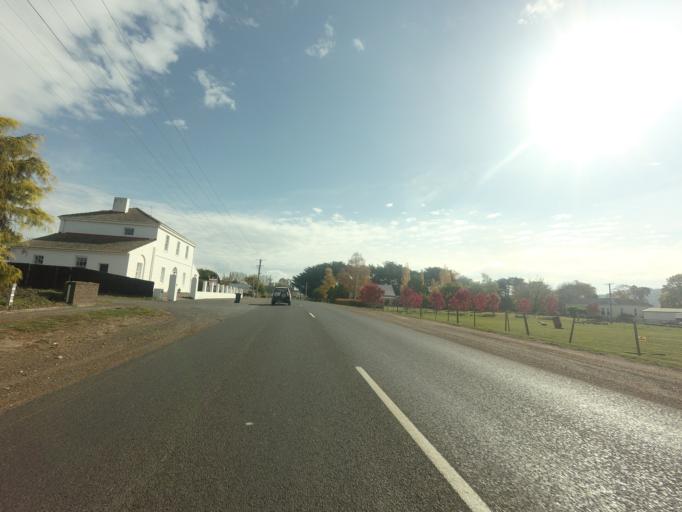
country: AU
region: Tasmania
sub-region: Meander Valley
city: Deloraine
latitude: -41.5211
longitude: 146.7375
